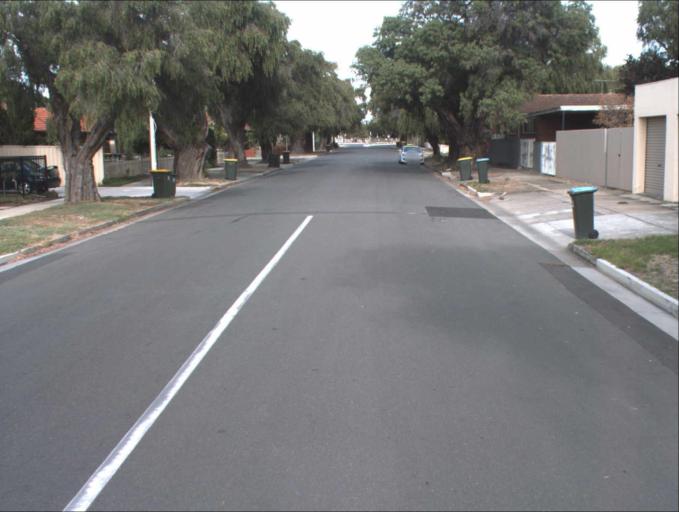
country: AU
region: South Australia
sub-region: Port Adelaide Enfield
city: Birkenhead
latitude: -34.8221
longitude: 138.4943
